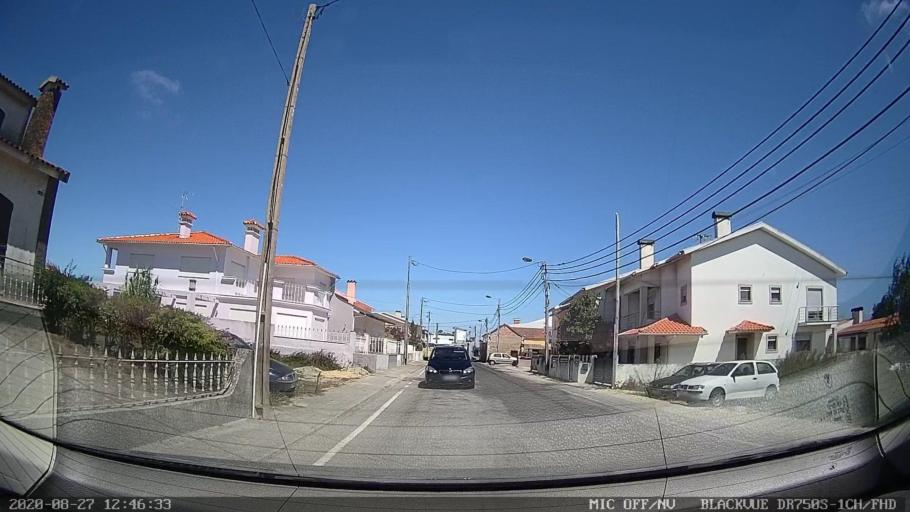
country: PT
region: Aveiro
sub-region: Ilhavo
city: Ilhavo
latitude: 40.6117
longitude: -8.6842
